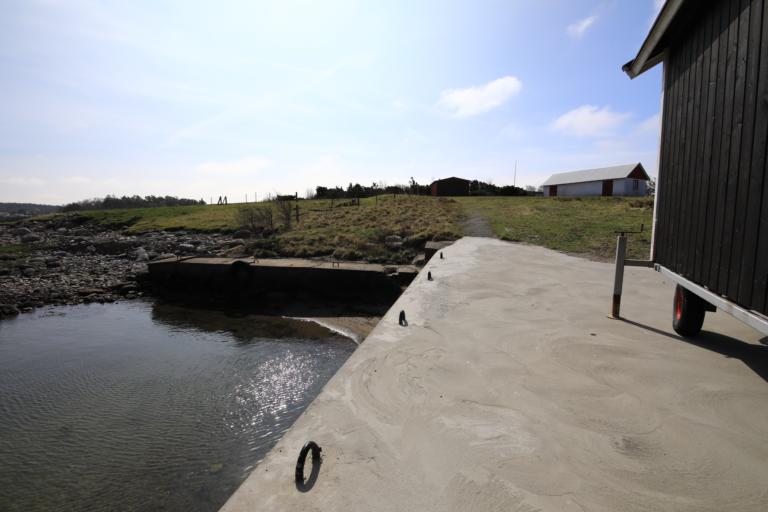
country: SE
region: Halland
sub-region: Kungsbacka Kommun
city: Frillesas
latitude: 57.2837
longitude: 12.1452
